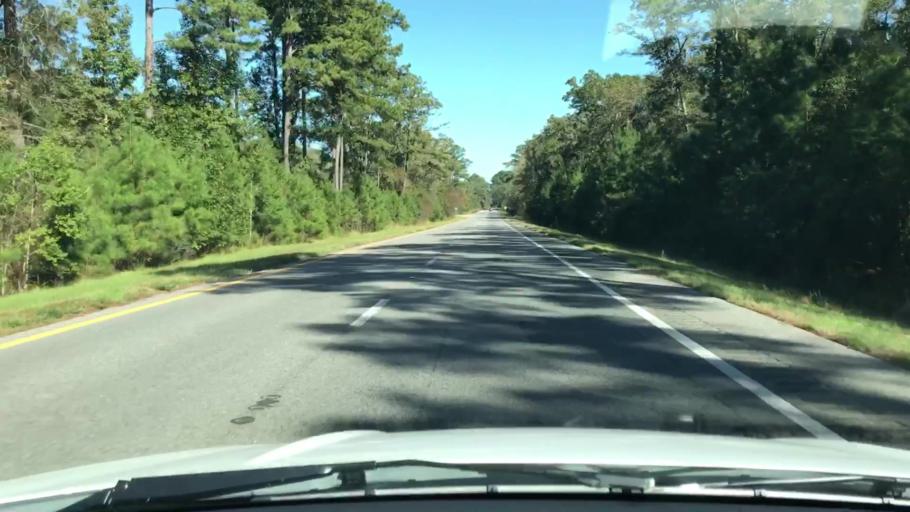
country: US
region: South Carolina
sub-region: Hampton County
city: Yemassee
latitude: 32.6455
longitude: -80.7025
